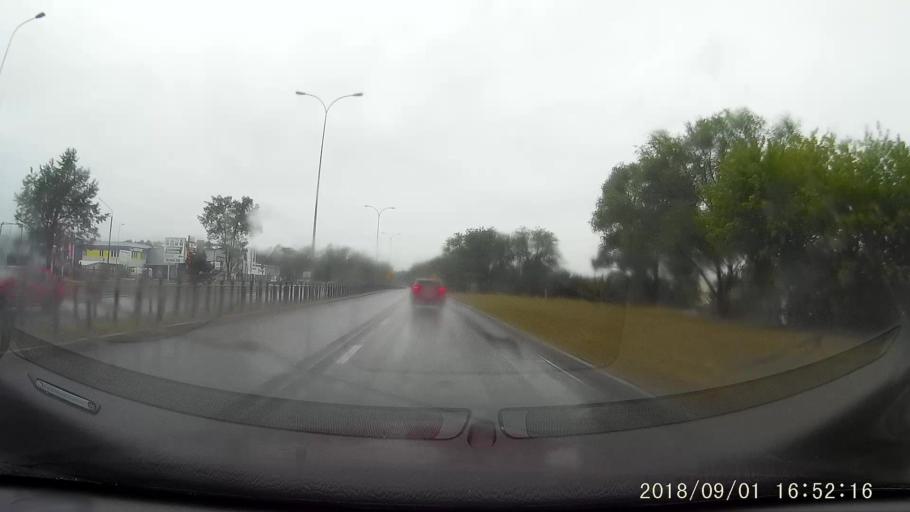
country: PL
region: Lubusz
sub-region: Zielona Gora
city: Zielona Gora
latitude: 51.9622
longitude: 15.4923
